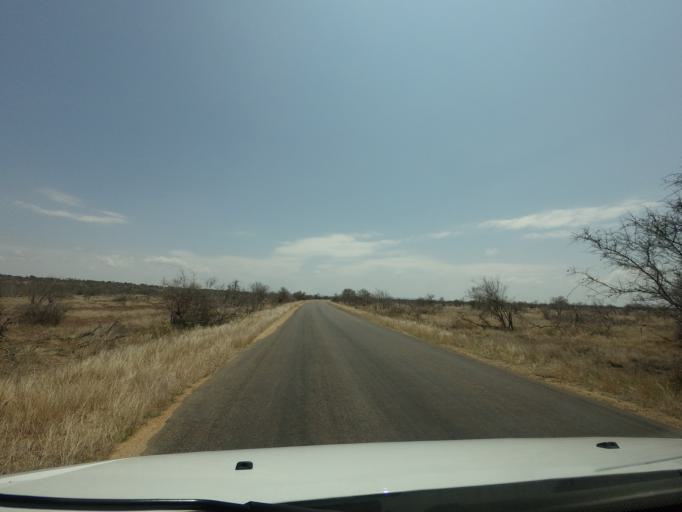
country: ZA
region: Limpopo
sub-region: Mopani District Municipality
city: Phalaborwa
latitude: -24.1111
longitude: 31.6905
